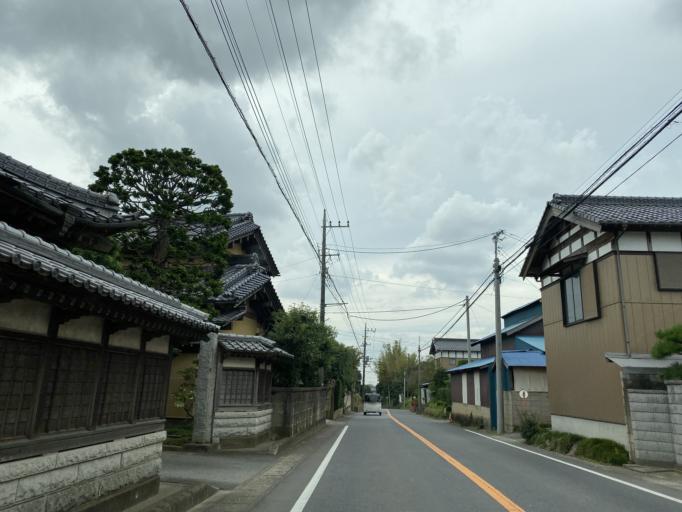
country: JP
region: Ibaraki
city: Moriya
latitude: 35.9812
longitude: 140.0420
